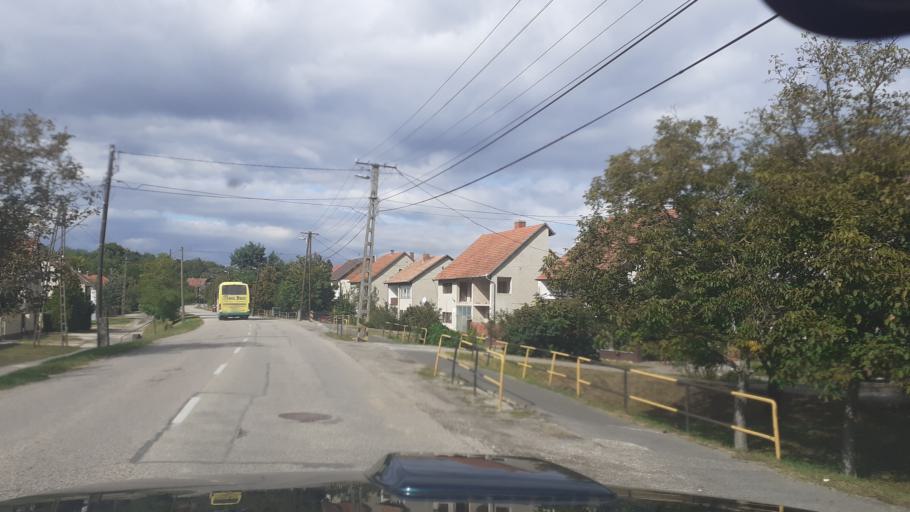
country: HU
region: Bacs-Kiskun
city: Solt
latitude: 46.8061
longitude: 18.9931
